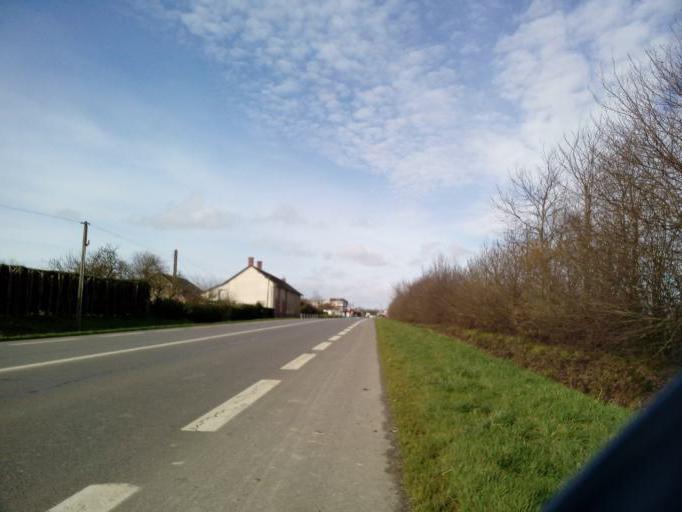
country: FR
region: Brittany
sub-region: Departement d'Ille-et-Vilaine
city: Montgermont
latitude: 48.1692
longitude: -1.7183
